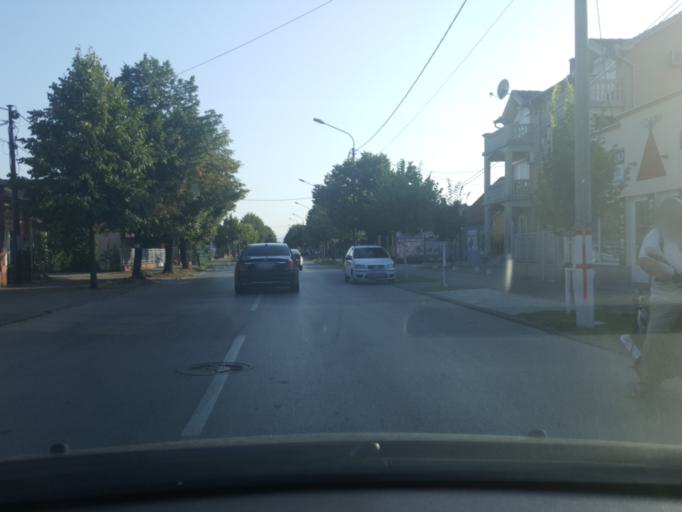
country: RS
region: Central Serbia
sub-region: Macvanski Okrug
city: Sabac
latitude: 44.7459
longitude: 19.7003
